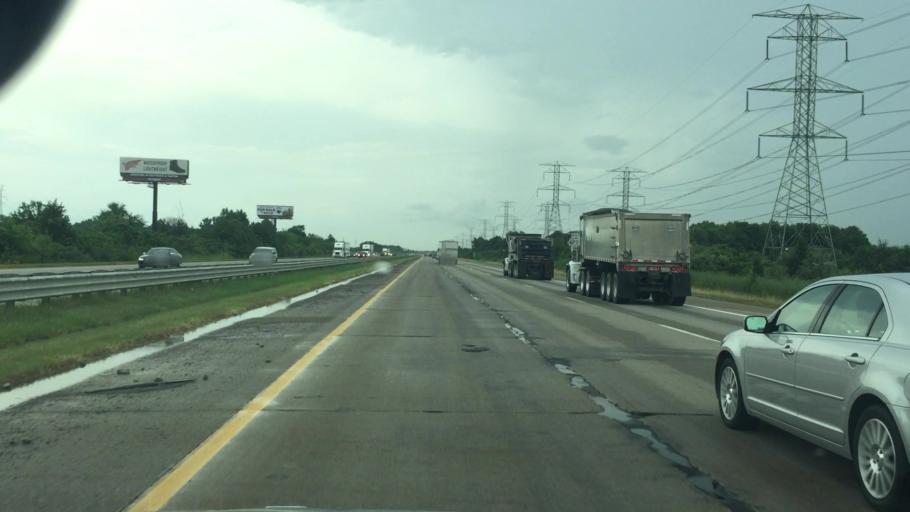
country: US
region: Michigan
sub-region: Monroe County
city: Woodland Beach
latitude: 42.0103
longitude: -83.3094
